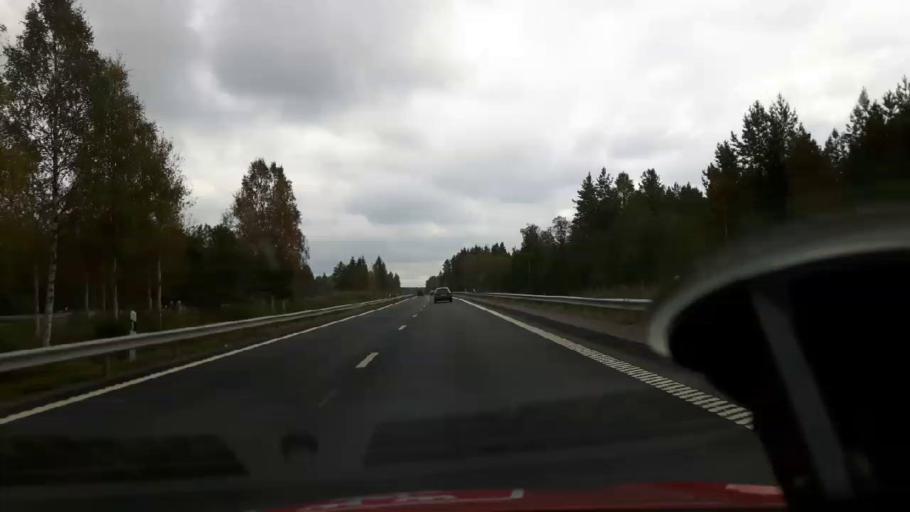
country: SE
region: Gaevleborg
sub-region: Gavle Kommun
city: Gavle
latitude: 60.6186
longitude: 17.1622
